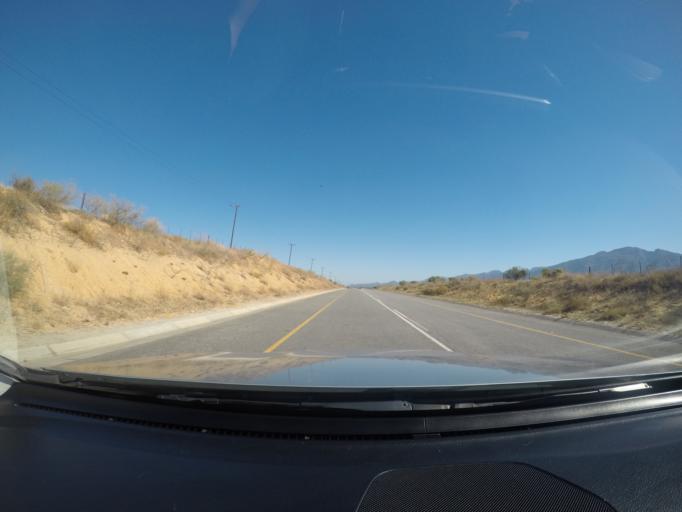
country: ZA
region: Western Cape
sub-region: West Coast District Municipality
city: Piketberg
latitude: -32.5934
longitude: 18.9895
